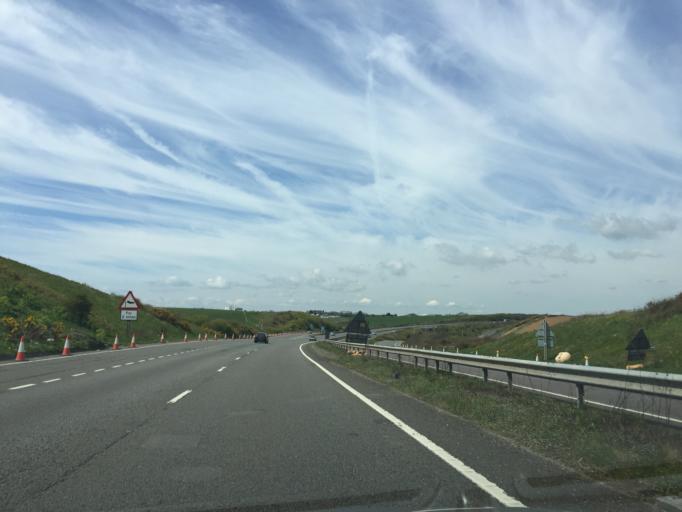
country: GB
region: England
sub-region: Kent
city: Dover
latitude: 51.1039
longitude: 1.2476
